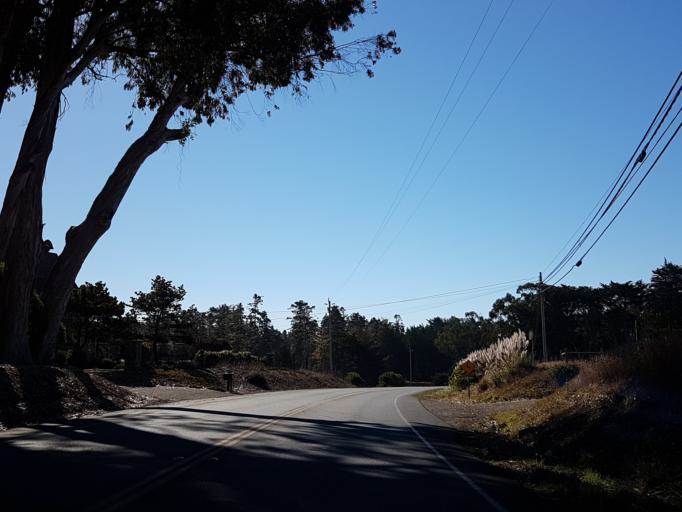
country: US
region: California
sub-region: Mendocino County
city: Fort Bragg
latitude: 39.2813
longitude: -123.7919
